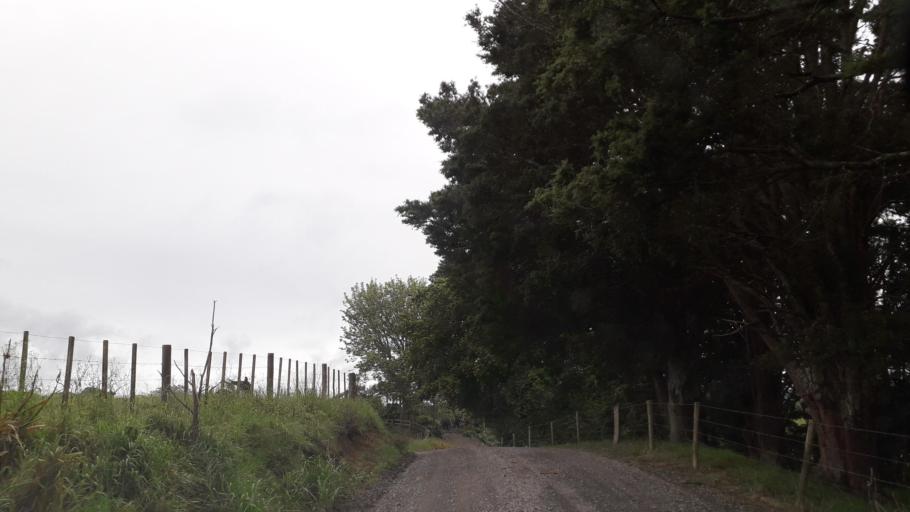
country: NZ
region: Northland
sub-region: Far North District
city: Waimate North
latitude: -35.3006
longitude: 173.5647
